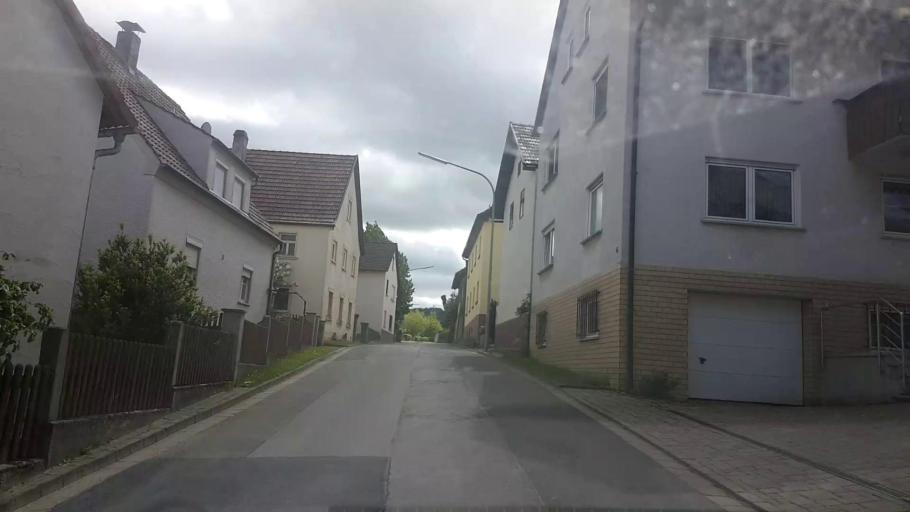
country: DE
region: Bavaria
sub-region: Upper Franconia
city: Bad Staffelstein
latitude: 50.1144
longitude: 11.0314
